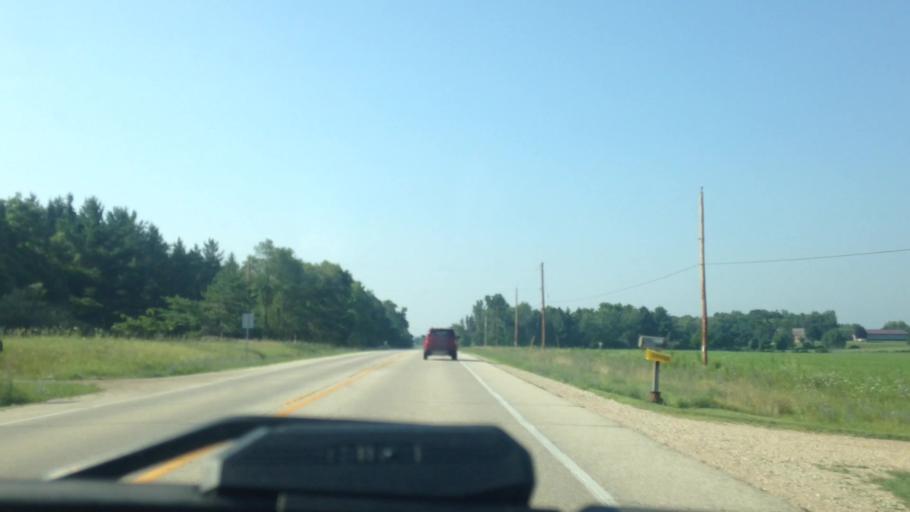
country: US
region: Wisconsin
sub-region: Washington County
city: Slinger
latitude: 43.2898
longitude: -88.2610
